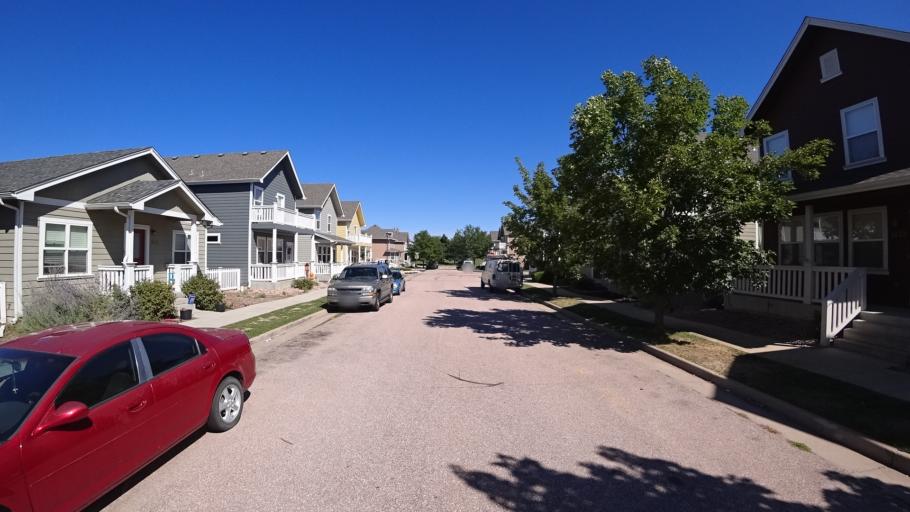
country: US
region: Colorado
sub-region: El Paso County
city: Stratmoor
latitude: 38.8110
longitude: -104.7354
